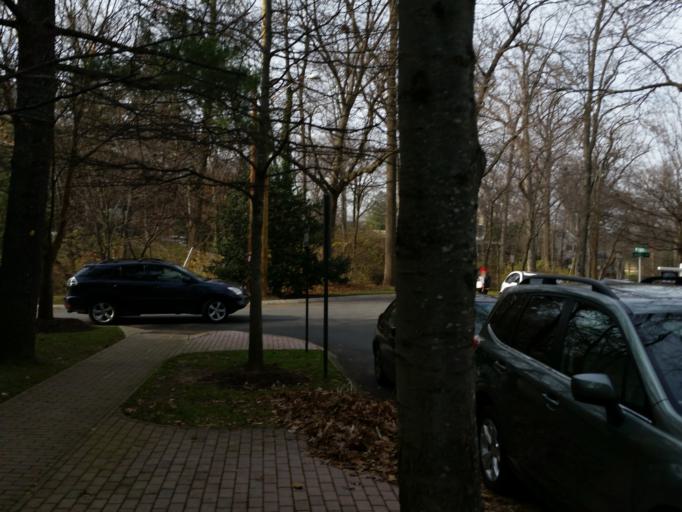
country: US
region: Maryland
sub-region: Montgomery County
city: Chevy Chase
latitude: 38.9712
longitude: -77.0778
